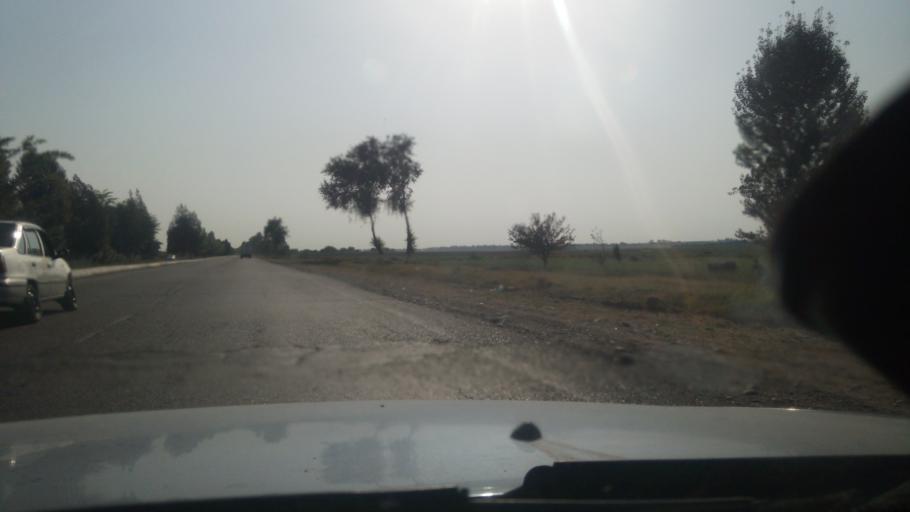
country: UZ
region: Toshkent
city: Zafar
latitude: 41.0065
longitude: 68.8312
